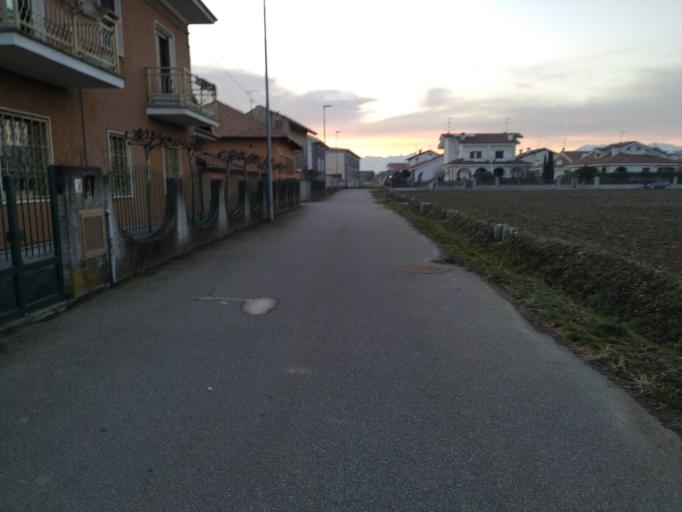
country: IT
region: Piedmont
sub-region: Provincia di Vercelli
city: Santhia
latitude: 45.3648
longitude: 8.1630
